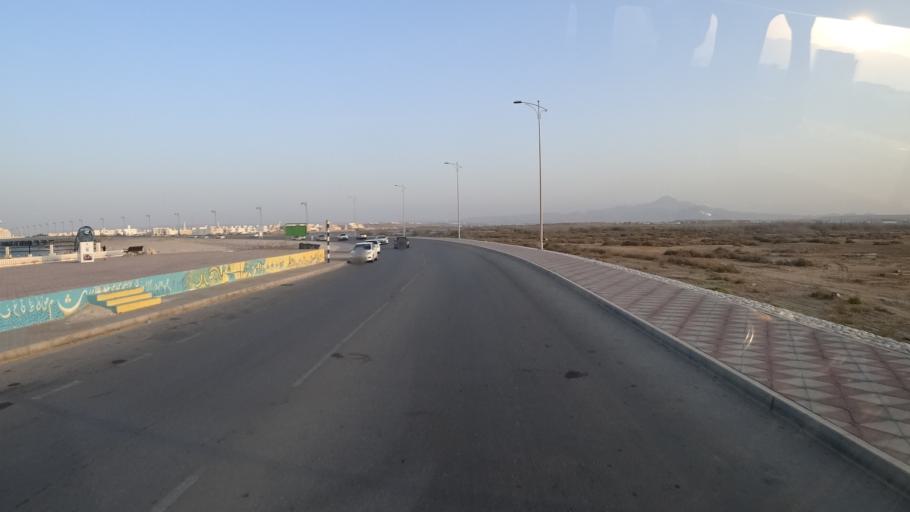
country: OM
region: Ash Sharqiyah
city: Sur
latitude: 22.6006
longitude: 59.4855
